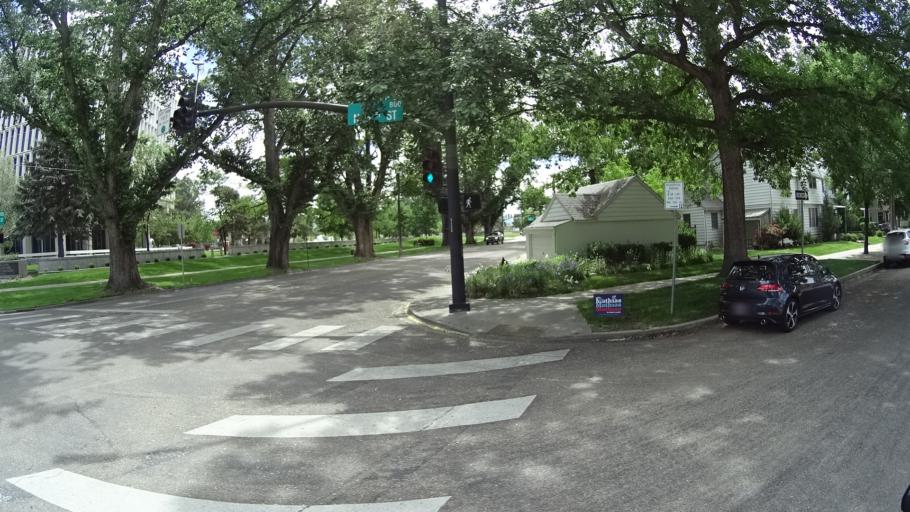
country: US
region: Idaho
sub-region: Ada County
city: Boise
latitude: 43.6203
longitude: -116.1955
